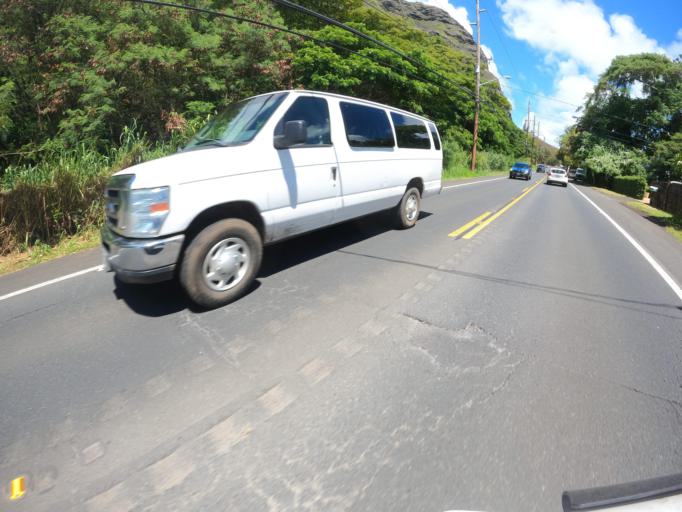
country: US
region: Hawaii
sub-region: Honolulu County
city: Ka'a'awa
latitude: 21.5316
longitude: -157.8370
